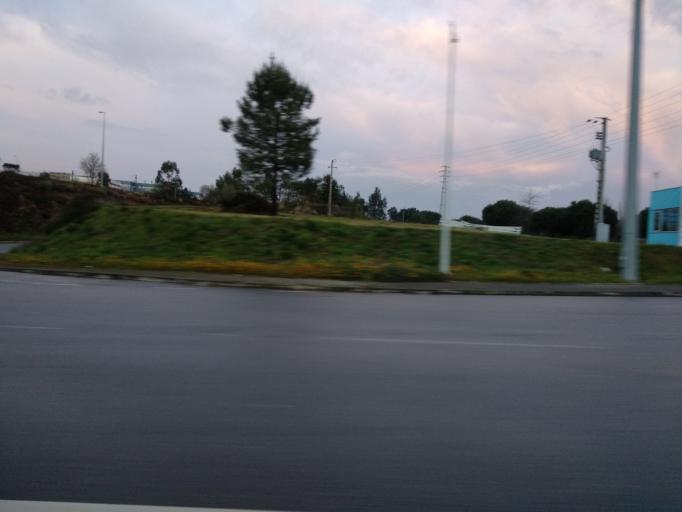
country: PT
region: Braga
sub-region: Vila Nova de Famalicao
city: Calendario
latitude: 41.3886
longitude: -8.5181
